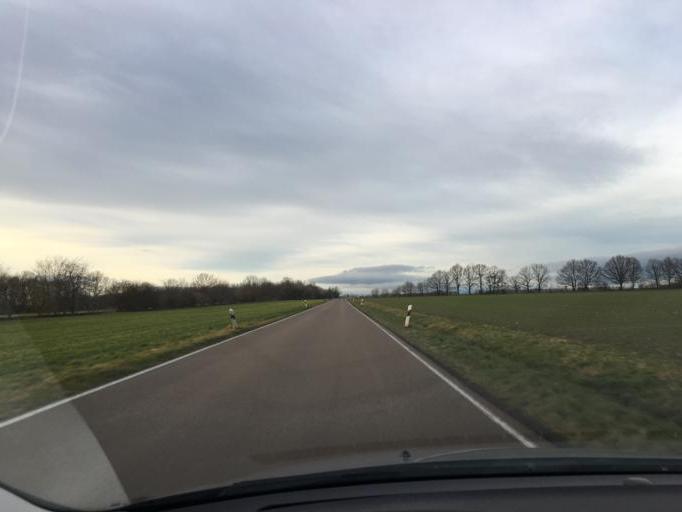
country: DE
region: Saxony
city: Grossposna
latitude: 51.2300
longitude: 12.4965
